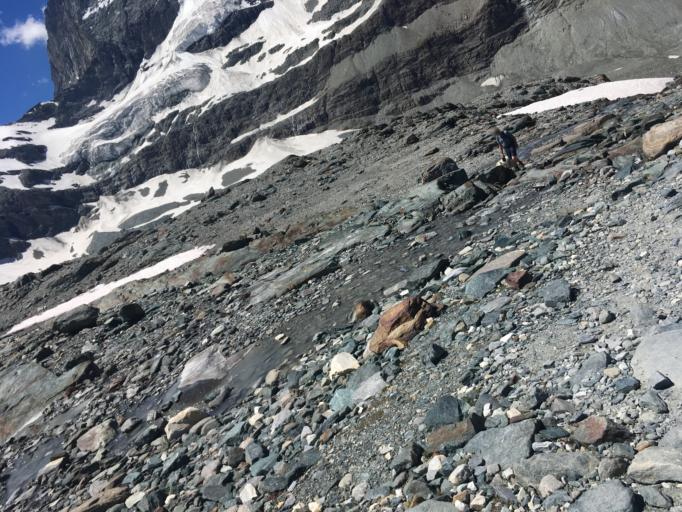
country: CH
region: Valais
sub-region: Visp District
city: Zermatt
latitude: 45.9750
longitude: 7.6967
